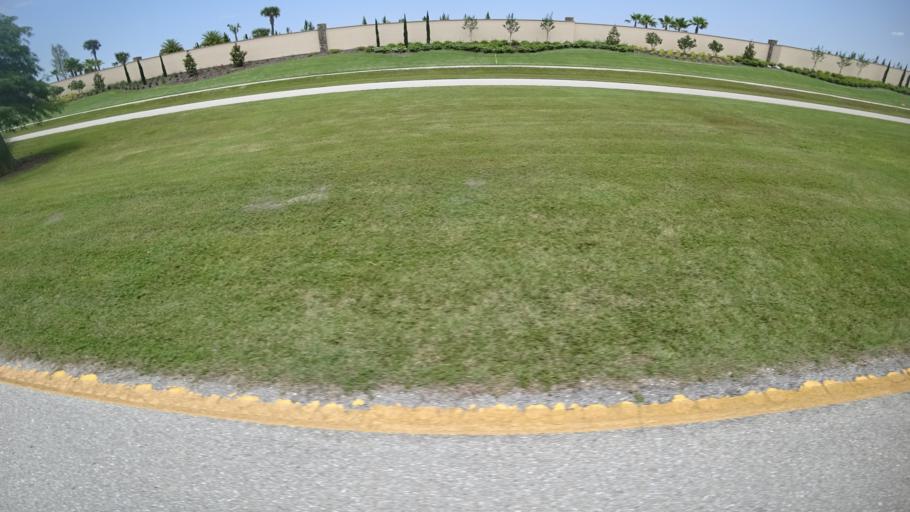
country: US
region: Florida
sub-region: Sarasota County
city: The Meadows
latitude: 27.3870
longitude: -82.3928
